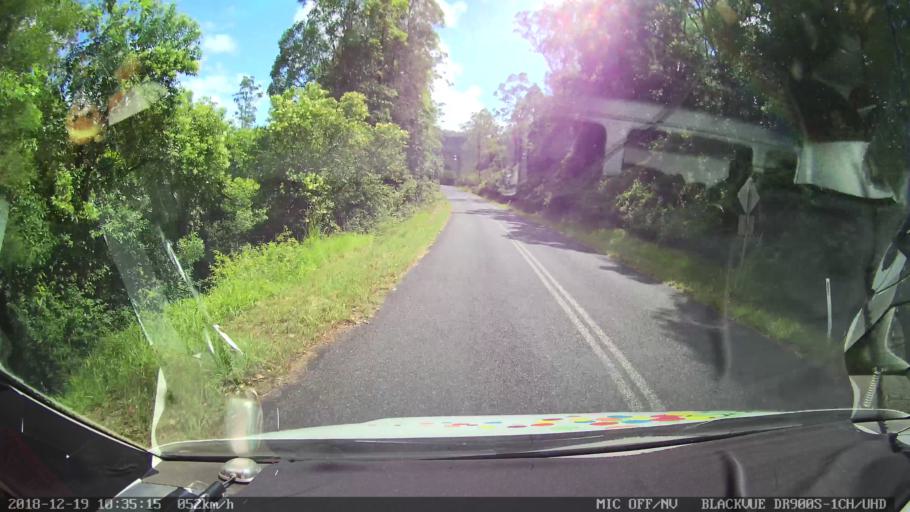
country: AU
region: New South Wales
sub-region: Lismore Municipality
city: Larnook
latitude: -28.5775
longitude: 153.1350
